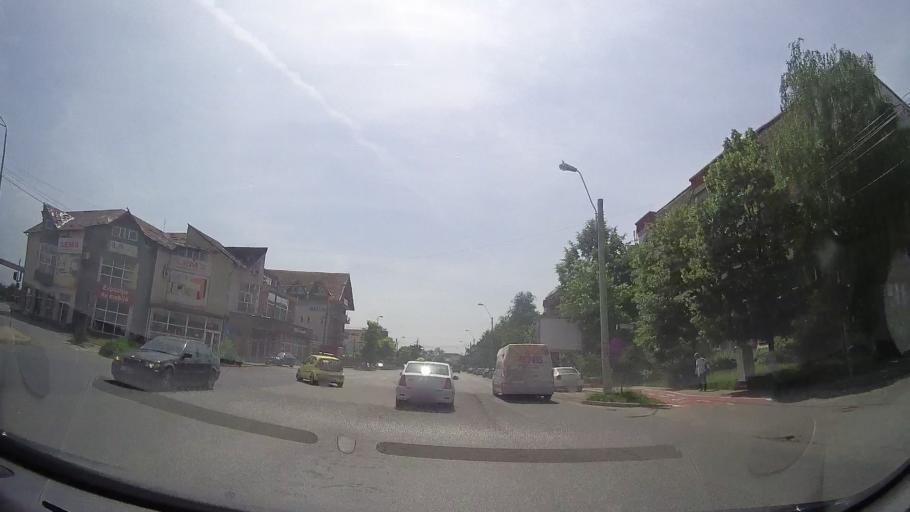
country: RO
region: Hunedoara
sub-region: Municipiul Deva
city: Deva
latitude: 45.8819
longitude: 22.9104
